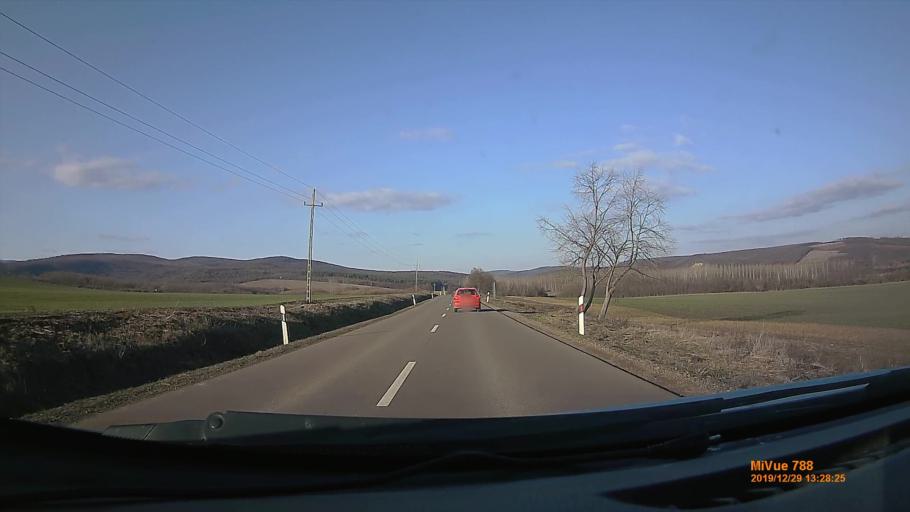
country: HU
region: Heves
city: Verpelet
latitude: 47.8622
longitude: 20.2038
